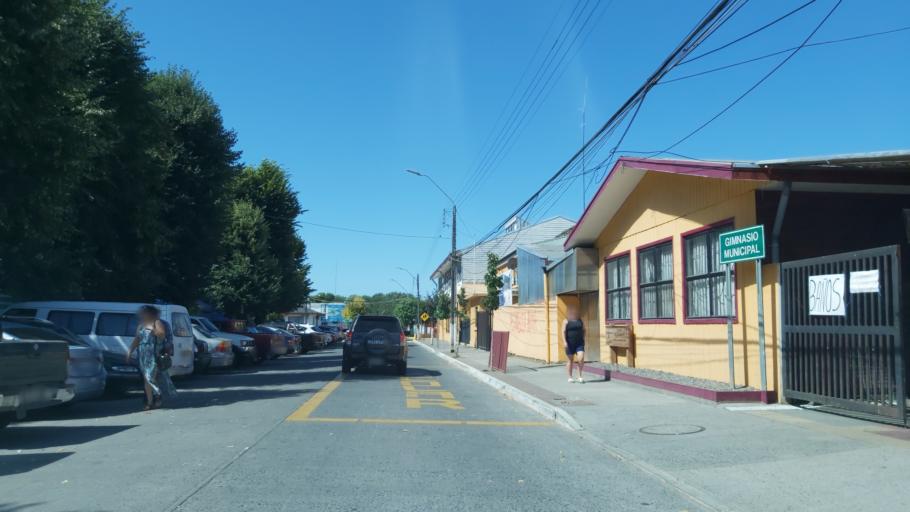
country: CL
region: Biobio
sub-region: Provincia de Concepcion
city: Lota
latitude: -37.1755
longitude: -72.9373
